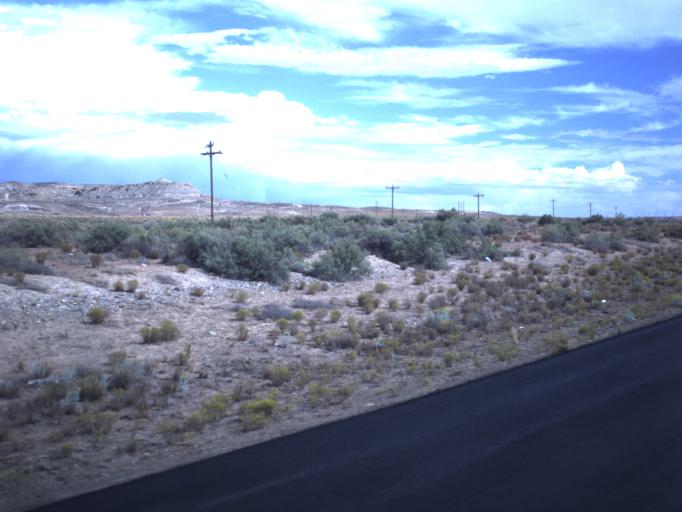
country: US
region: Utah
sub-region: San Juan County
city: Blanding
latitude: 37.2468
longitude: -109.2545
